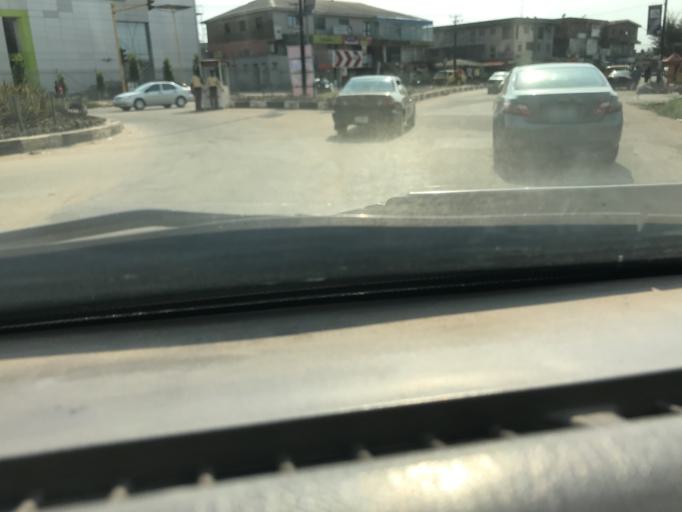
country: NG
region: Lagos
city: Agege
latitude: 6.6028
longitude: 3.3095
